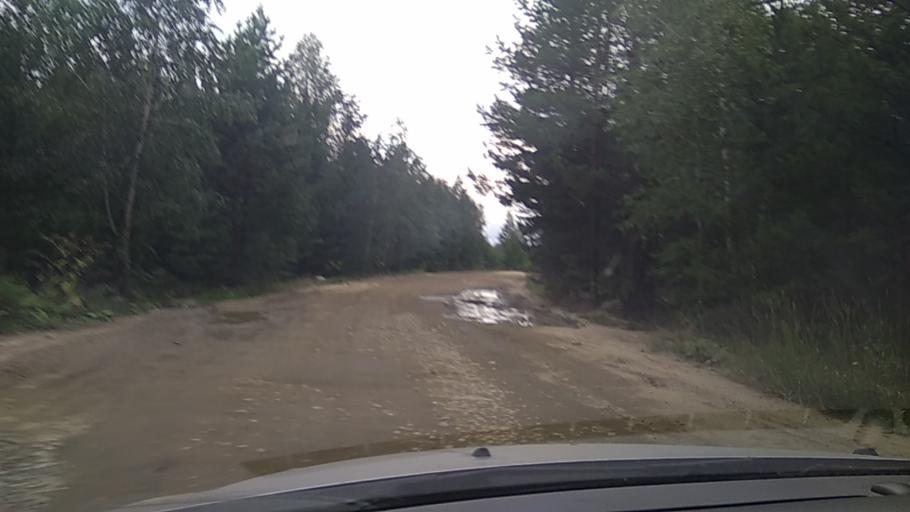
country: RU
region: Chelyabinsk
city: Kyshtym
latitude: 55.6805
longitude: 60.5737
